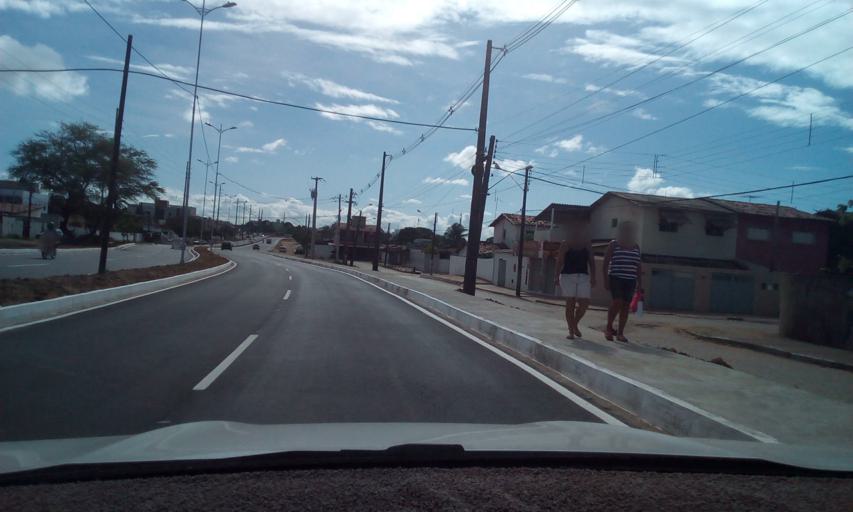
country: BR
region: Paraiba
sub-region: Conde
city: Conde
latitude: -7.2074
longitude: -34.8487
